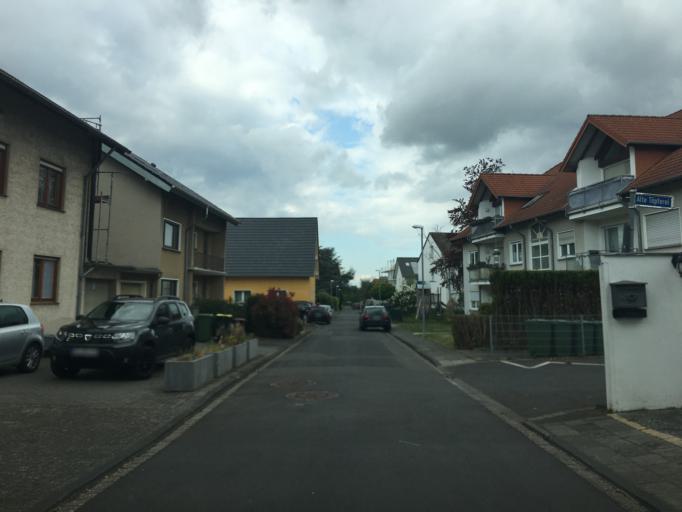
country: DE
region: North Rhine-Westphalia
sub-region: Regierungsbezirk Koln
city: Rheinbach
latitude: 50.6261
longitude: 6.9577
